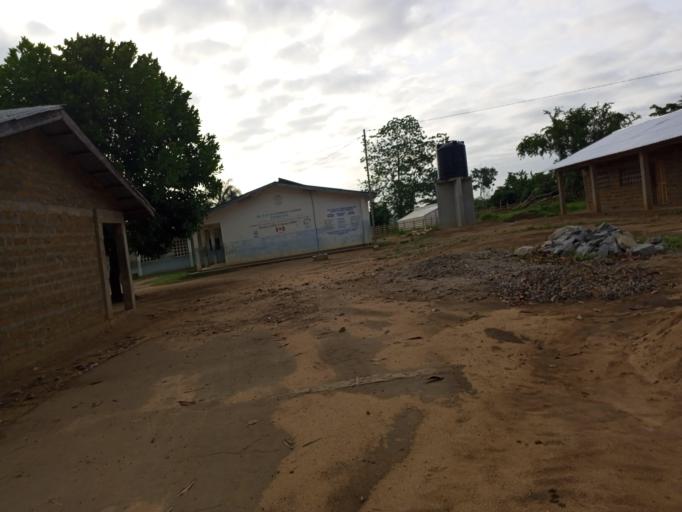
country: SL
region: Eastern Province
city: Pendembu
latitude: 8.1079
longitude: -10.6918
